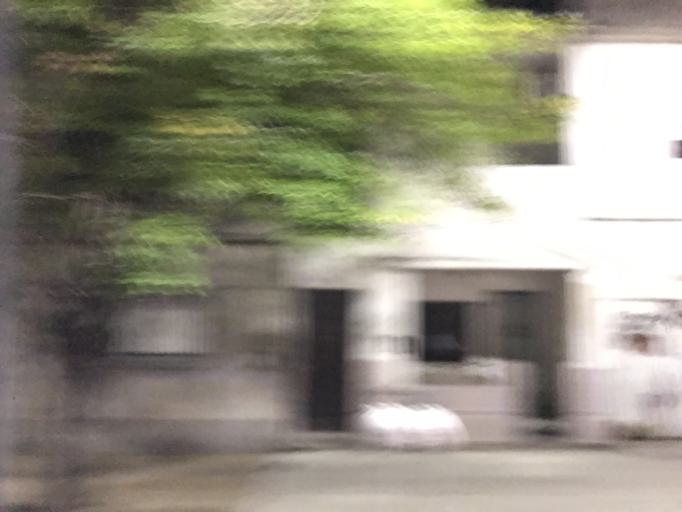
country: AR
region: Buenos Aires
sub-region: Partido de Lanus
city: Lanus
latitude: -34.6767
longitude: -58.4104
